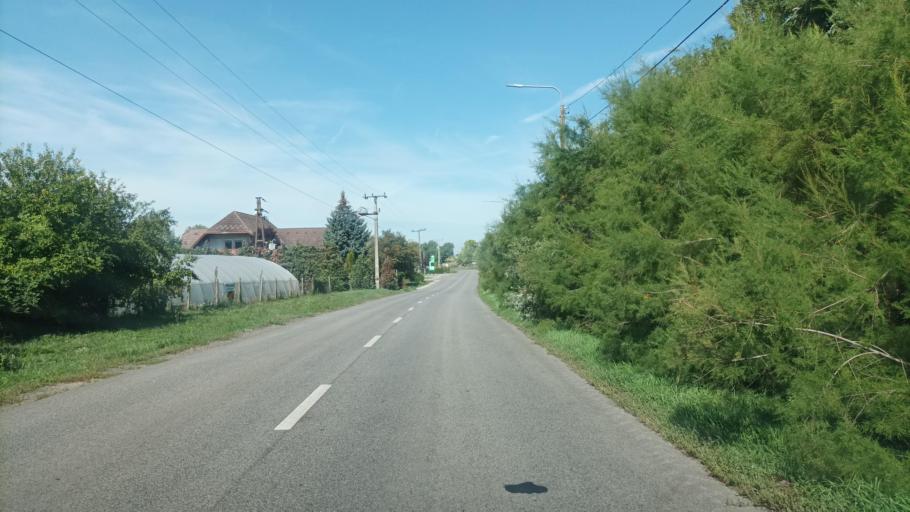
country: HU
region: Pest
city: Zsambok
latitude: 47.5485
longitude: 19.6004
